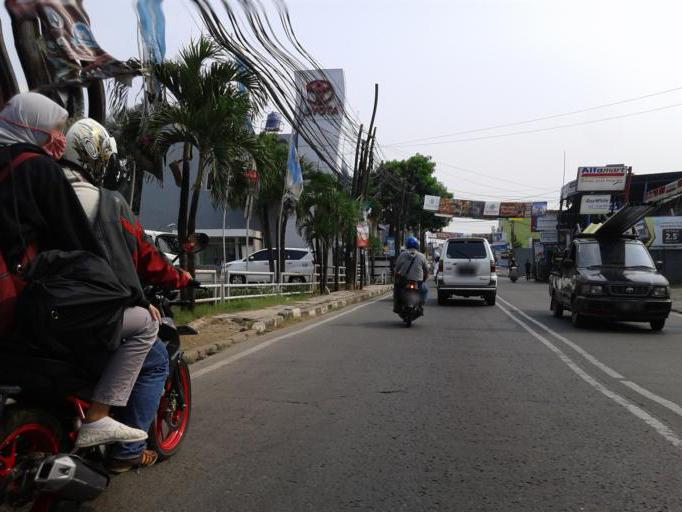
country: ID
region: West Java
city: Pamulang
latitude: -6.3304
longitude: 106.7840
